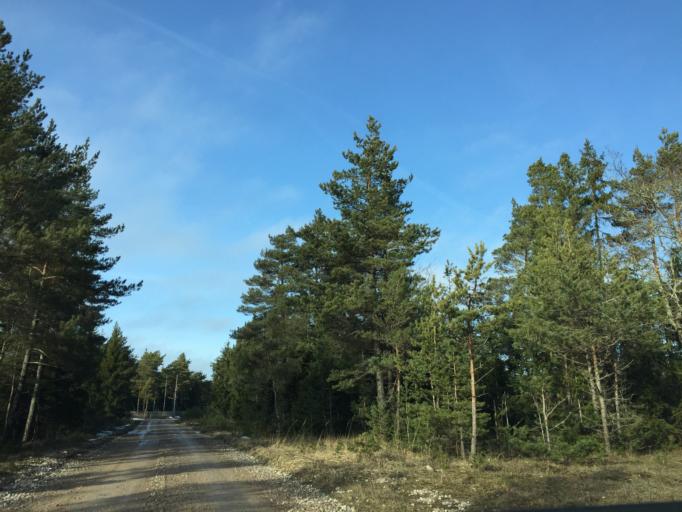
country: EE
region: Saare
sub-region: Kuressaare linn
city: Kuressaare
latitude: 58.4802
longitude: 21.9490
